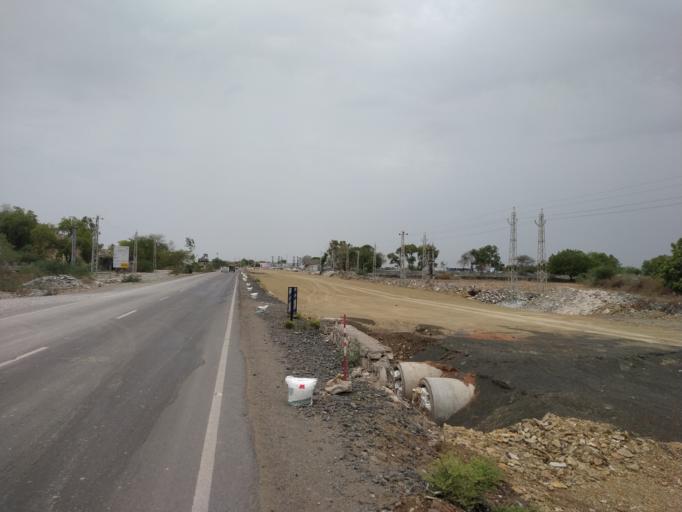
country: IN
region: Rajasthan
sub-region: Kota
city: Udpura
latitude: 24.7766
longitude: 75.9858
